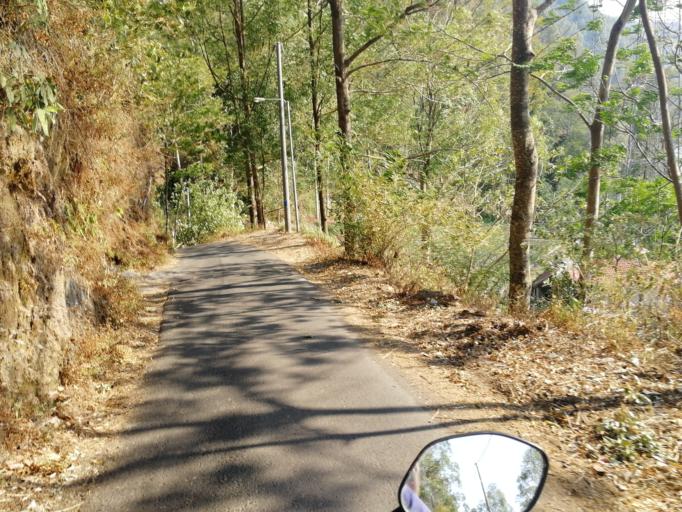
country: ID
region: Bali
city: Banjar Trunyan
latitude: -8.2584
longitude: 115.4239
